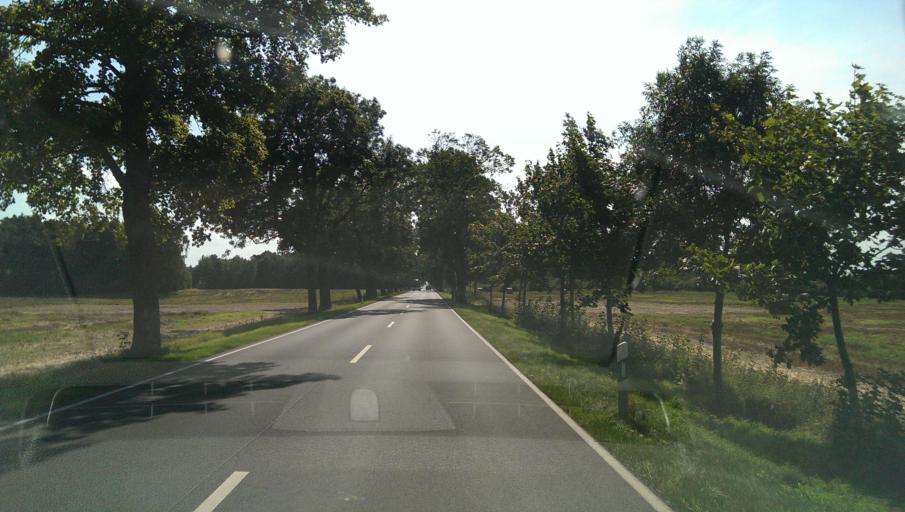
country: DE
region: Saxony-Anhalt
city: Abtsdorf
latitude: 51.9076
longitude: 12.6835
